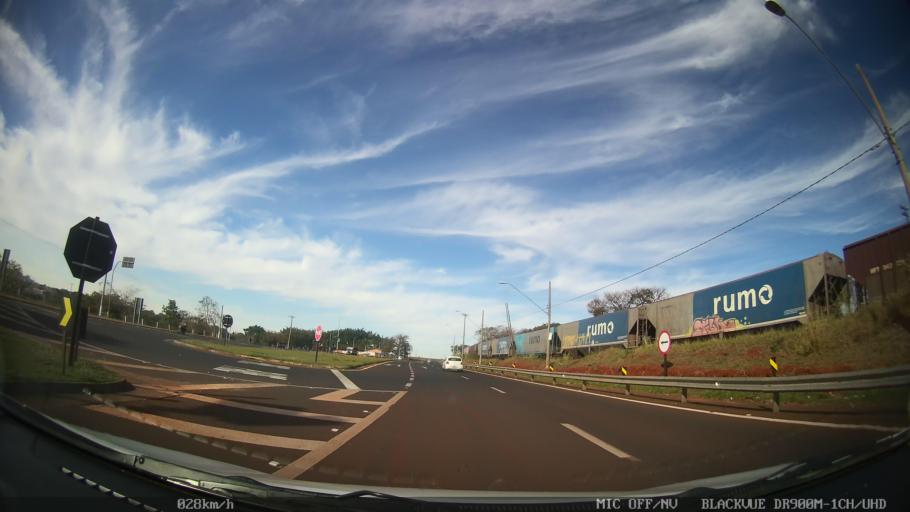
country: BR
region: Sao Paulo
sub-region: Araraquara
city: Araraquara
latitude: -21.7896
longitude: -48.1388
